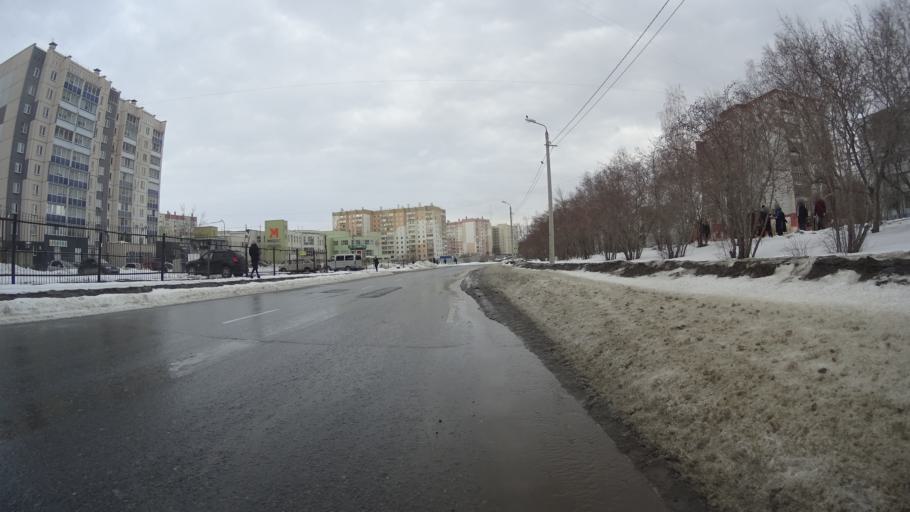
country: RU
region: Chelyabinsk
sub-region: Gorod Chelyabinsk
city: Chelyabinsk
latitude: 55.1970
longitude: 61.3214
